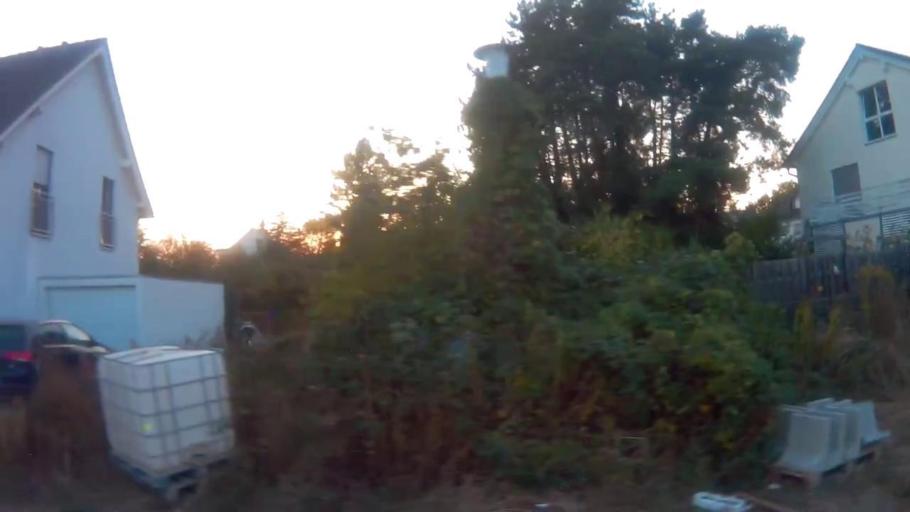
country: DE
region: Hesse
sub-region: Regierungsbezirk Darmstadt
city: Darmstadt
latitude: 49.8249
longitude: 8.6495
